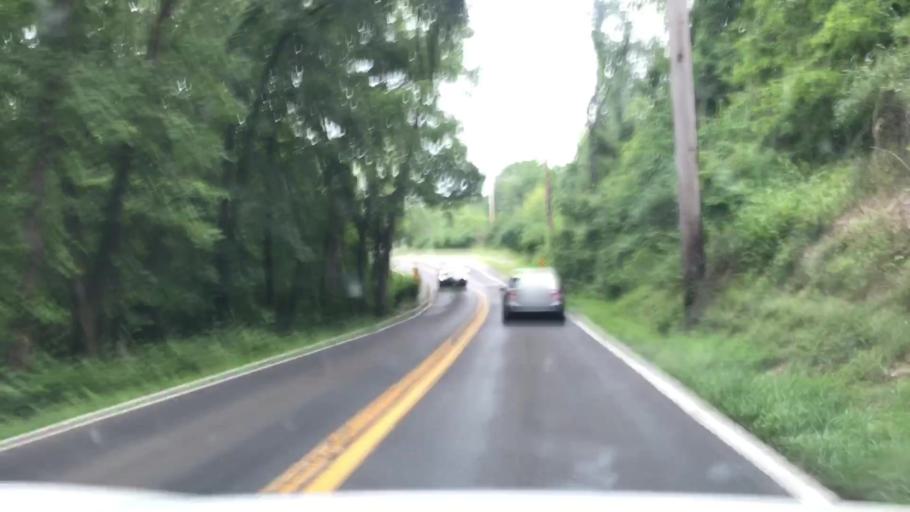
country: US
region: Missouri
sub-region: Saint Louis County
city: Clarkson Valley
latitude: 38.6488
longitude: -90.6159
